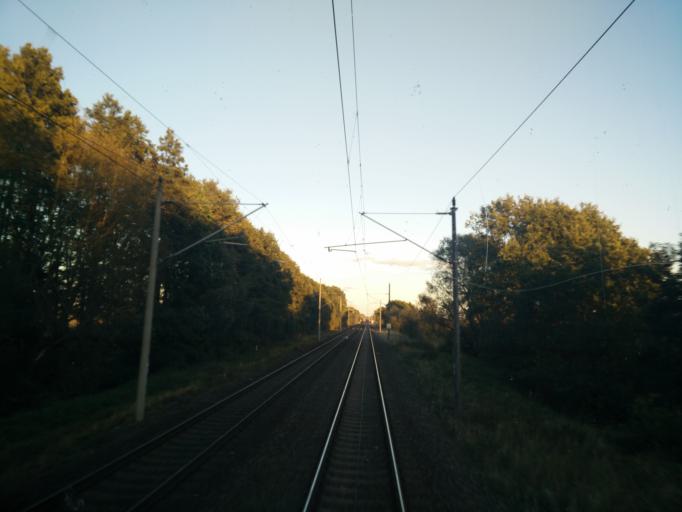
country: DE
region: Brandenburg
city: Breese
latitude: 52.9921
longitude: 11.7998
